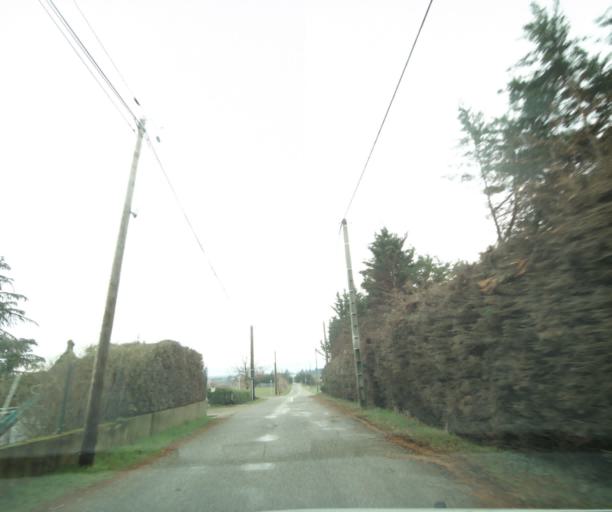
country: FR
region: Rhone-Alpes
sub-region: Departement de l'Ardeche
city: Cornas
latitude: 44.9748
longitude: 4.8758
